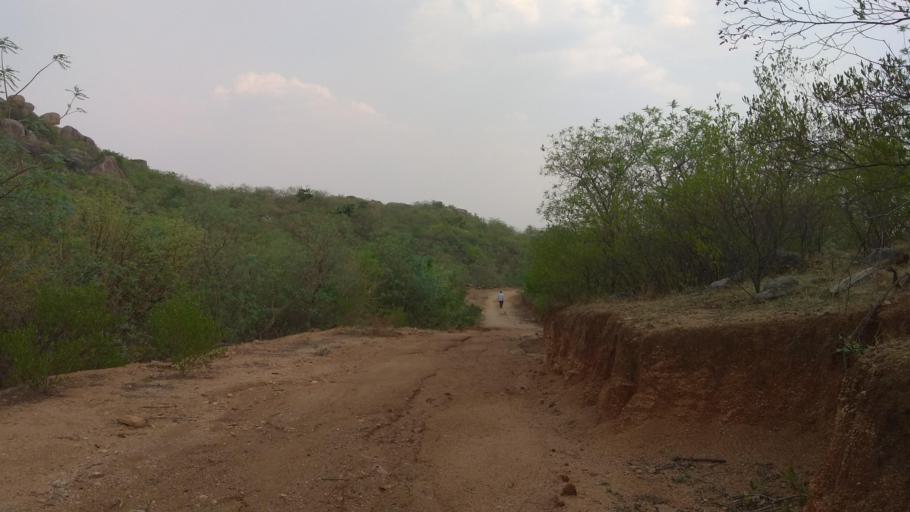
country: IN
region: Telangana
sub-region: Mahbubnagar
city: Farrukhnagar
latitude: 16.8920
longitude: 78.4971
